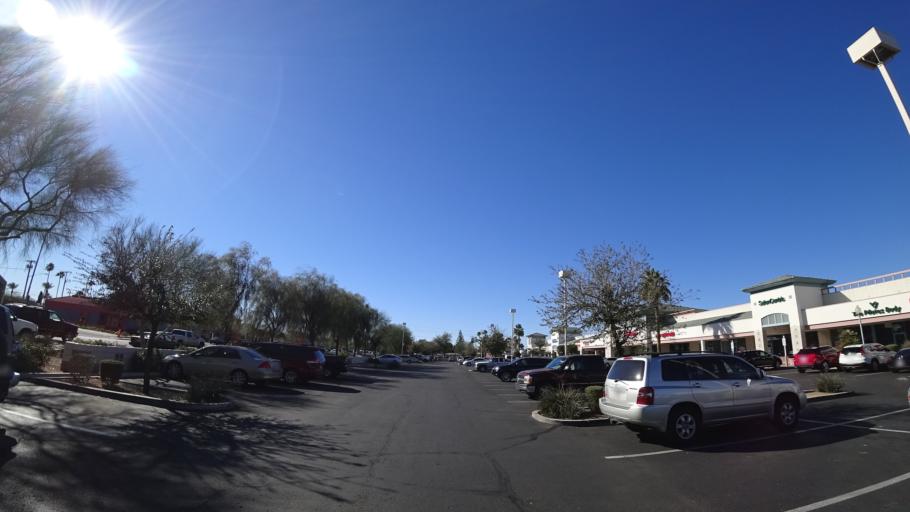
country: US
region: Arizona
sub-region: Maricopa County
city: Phoenix
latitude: 33.5385
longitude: -112.0634
